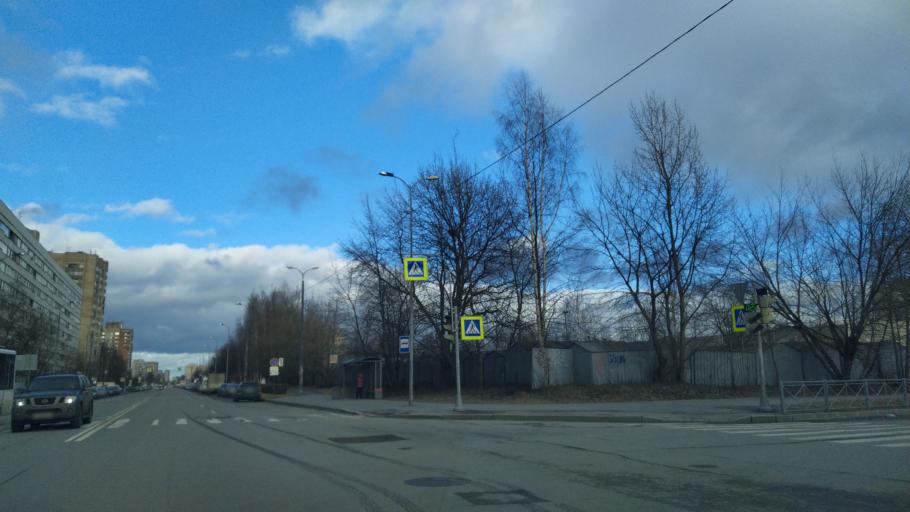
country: RU
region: St.-Petersburg
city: Grazhdanka
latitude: 60.0365
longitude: 30.3817
